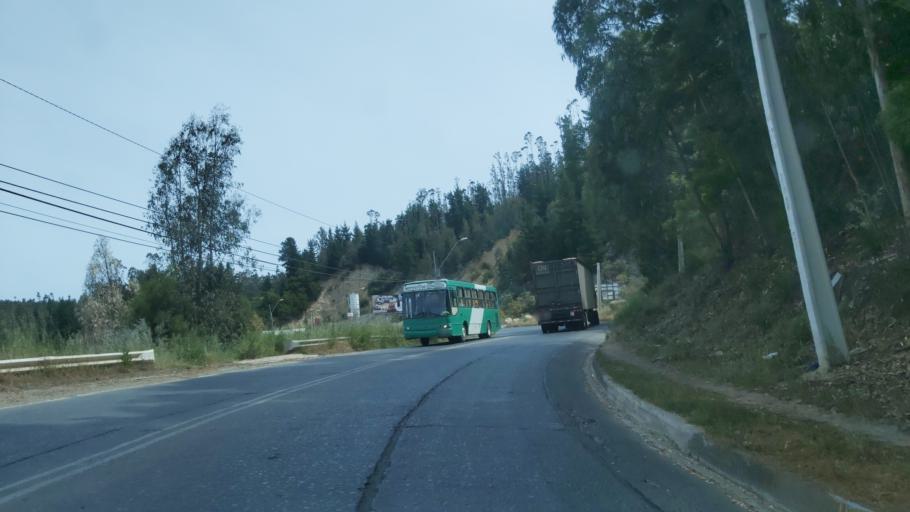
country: CL
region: Maule
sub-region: Provincia de Talca
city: Constitucion
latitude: -35.3469
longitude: -72.4133
